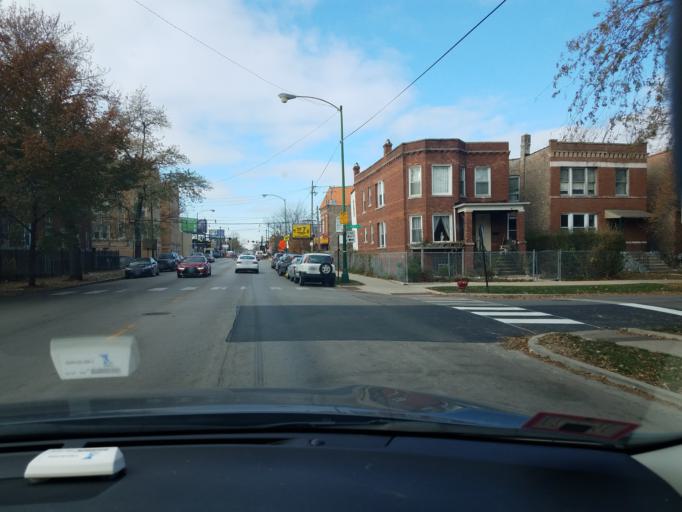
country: US
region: Illinois
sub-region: Cook County
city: Lincolnwood
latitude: 41.9463
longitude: -87.7336
